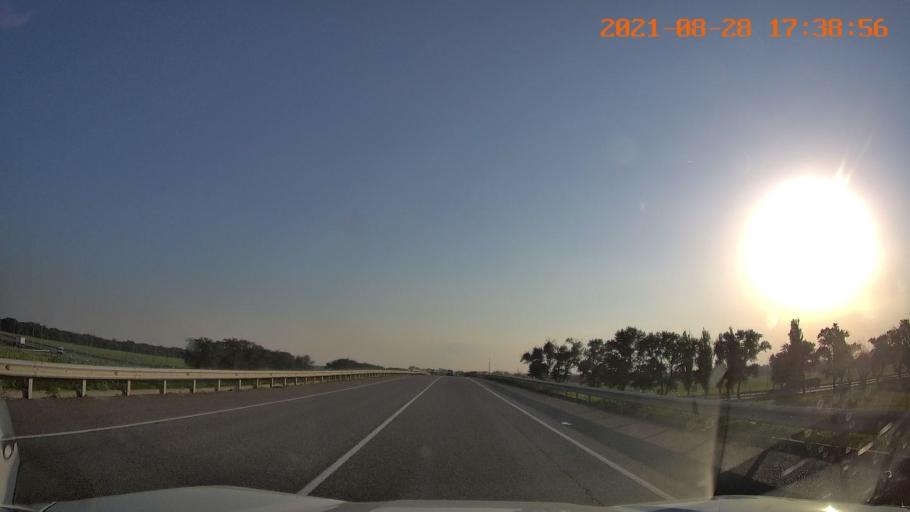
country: RU
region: Krasnodarskiy
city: Novokubansk
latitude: 45.0599
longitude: 40.9856
